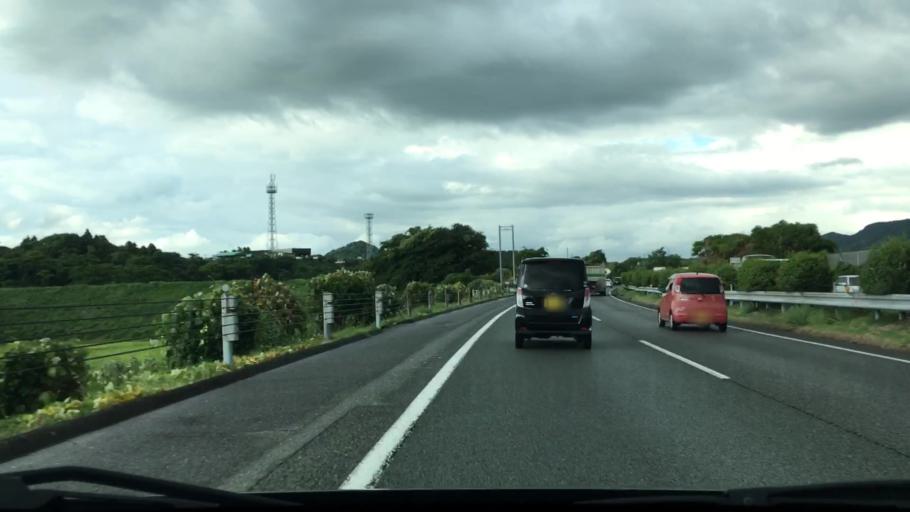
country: JP
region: Fukuoka
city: Koga
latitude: 33.7312
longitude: 130.5072
